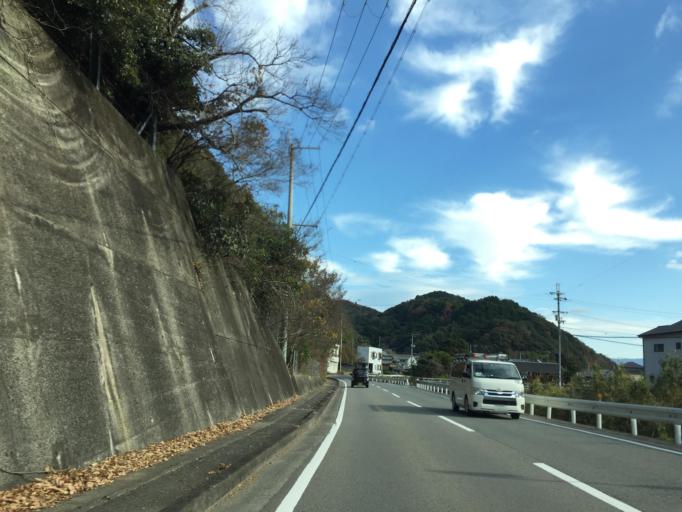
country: JP
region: Wakayama
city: Kainan
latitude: 34.1633
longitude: 135.2547
